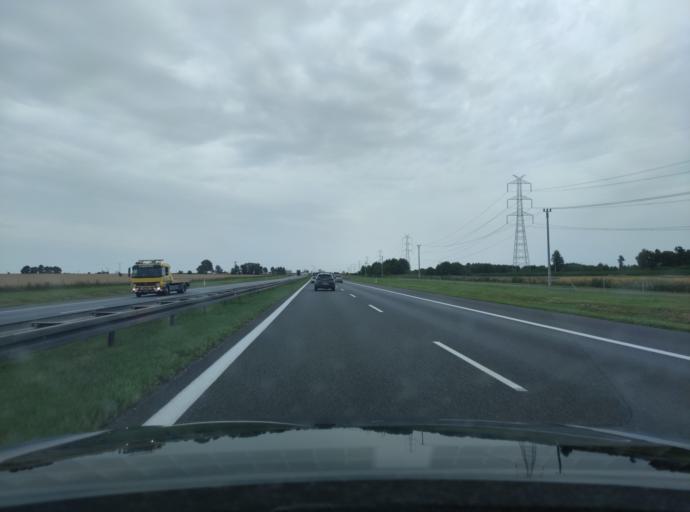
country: PL
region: Opole Voivodeship
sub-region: Powiat brzeski
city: Olszanka
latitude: 50.7609
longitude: 17.4220
